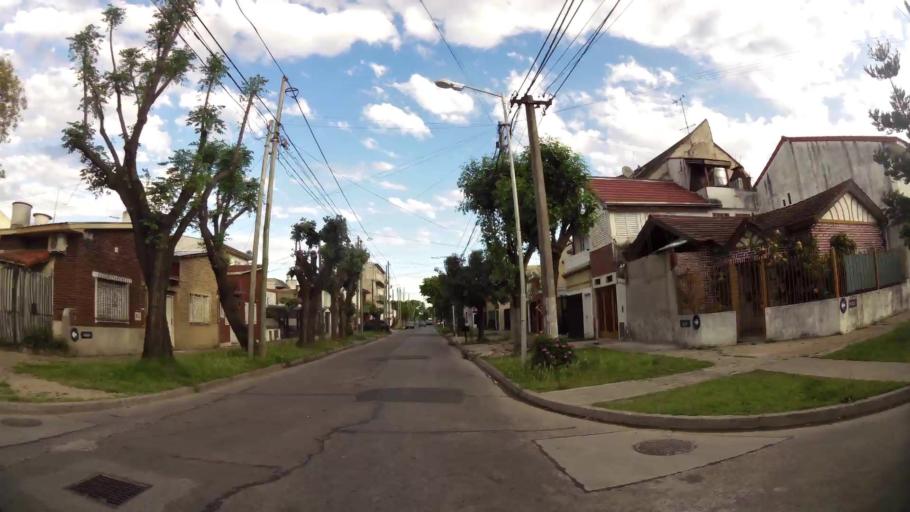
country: AR
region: Buenos Aires
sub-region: Partido de Avellaneda
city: Avellaneda
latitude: -34.6944
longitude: -58.3388
